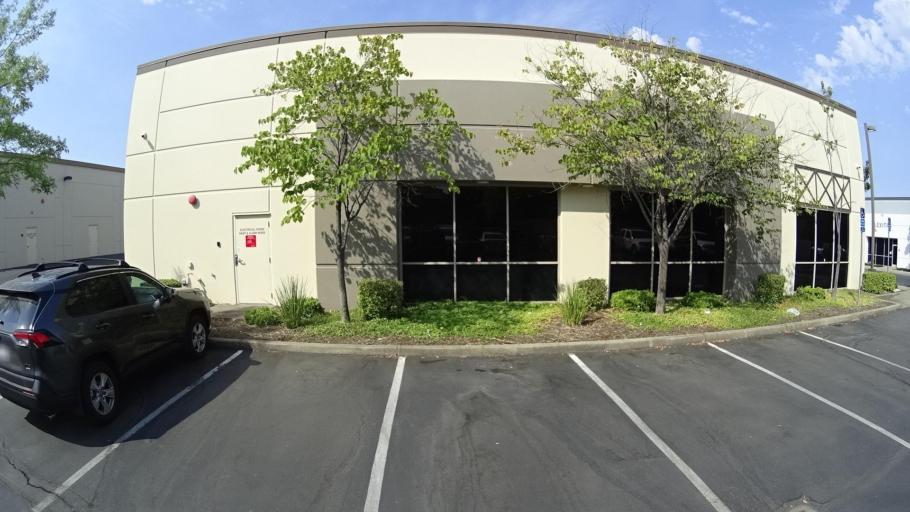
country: US
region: California
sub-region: Placer County
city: Rocklin
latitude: 38.7983
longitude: -121.2154
